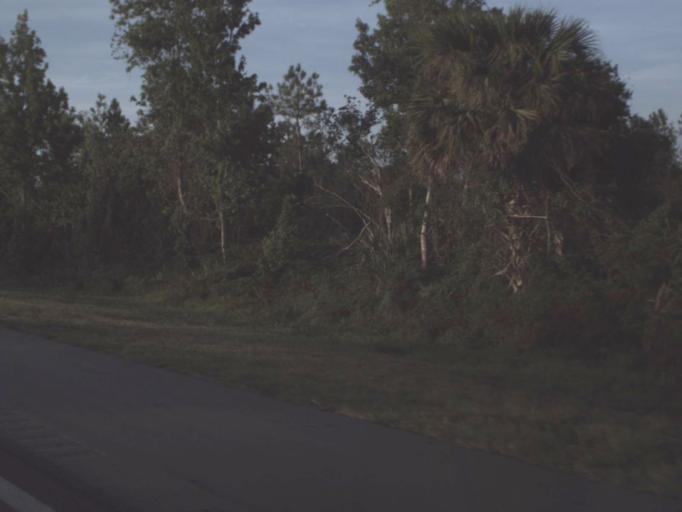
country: US
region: Florida
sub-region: Volusia County
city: Oak Hill
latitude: 28.7902
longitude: -80.8991
